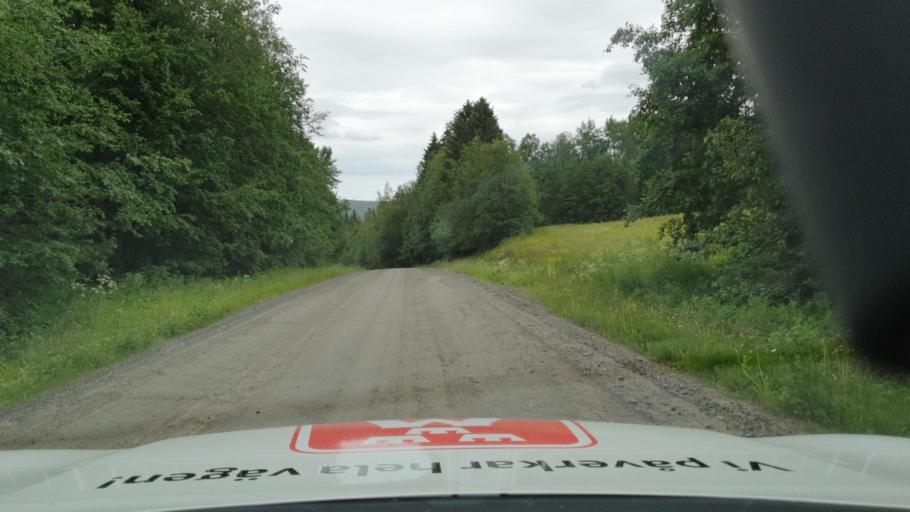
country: SE
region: Vaesterbotten
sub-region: Bjurholms Kommun
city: Bjurholm
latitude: 63.7909
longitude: 19.3679
